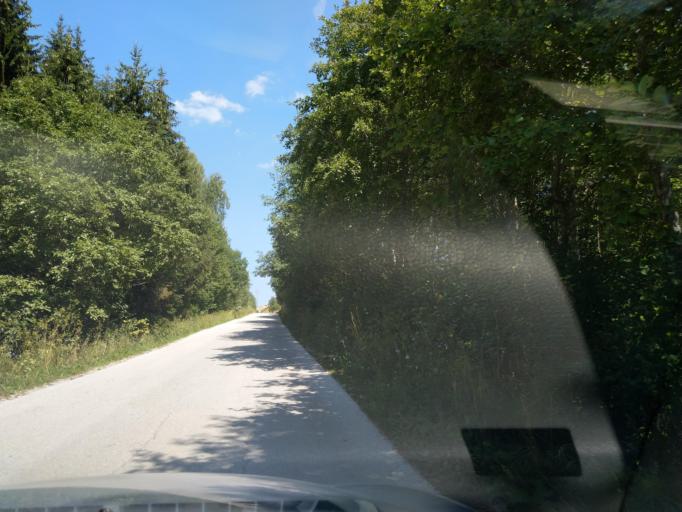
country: RS
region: Central Serbia
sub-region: Zlatiborski Okrug
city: Nova Varos
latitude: 43.4614
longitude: 19.9756
